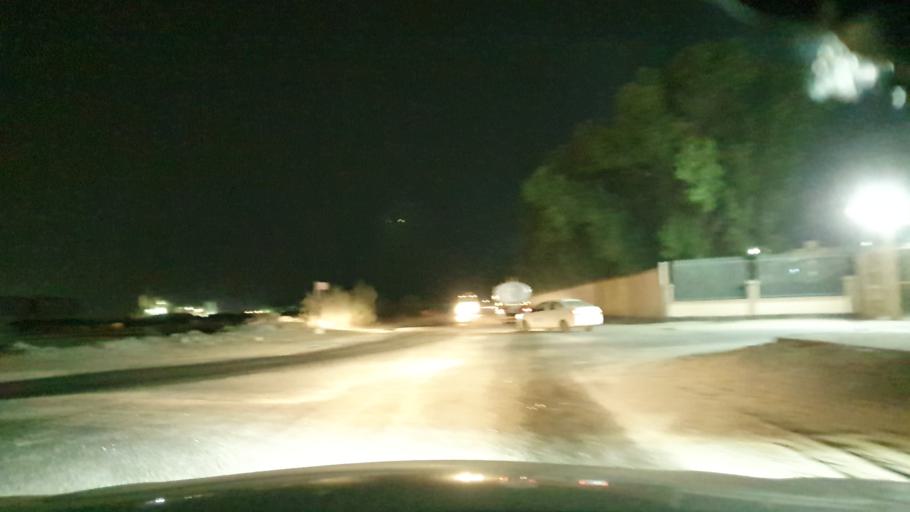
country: BH
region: Northern
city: Sitrah
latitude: 26.0848
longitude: 50.6130
